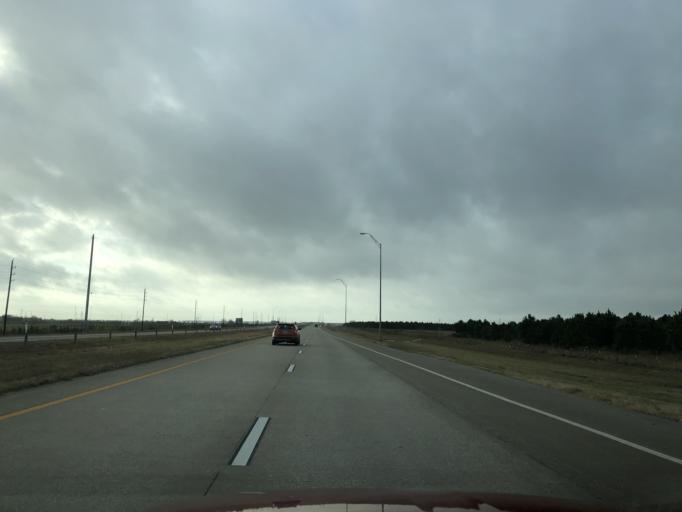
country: US
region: Texas
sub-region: Harris County
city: Cypress
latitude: 29.9338
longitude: -95.7636
